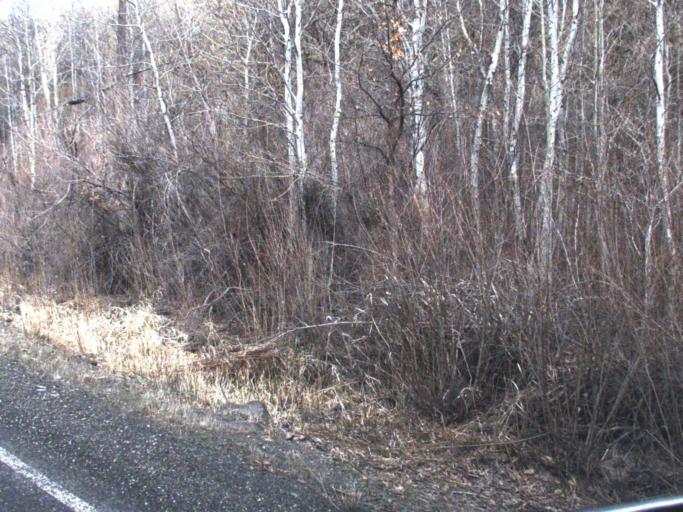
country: US
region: Washington
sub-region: Yakima County
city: Tieton
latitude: 46.7700
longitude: -120.8438
